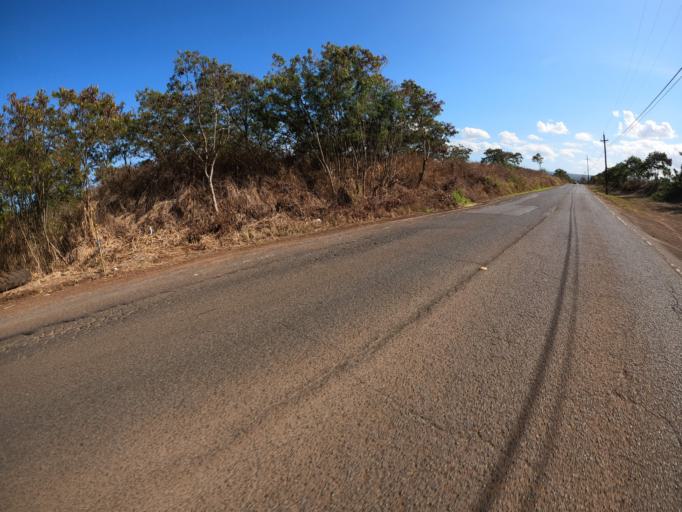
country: US
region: Hawaii
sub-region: Honolulu County
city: Waialua
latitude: 21.5705
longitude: -158.1396
